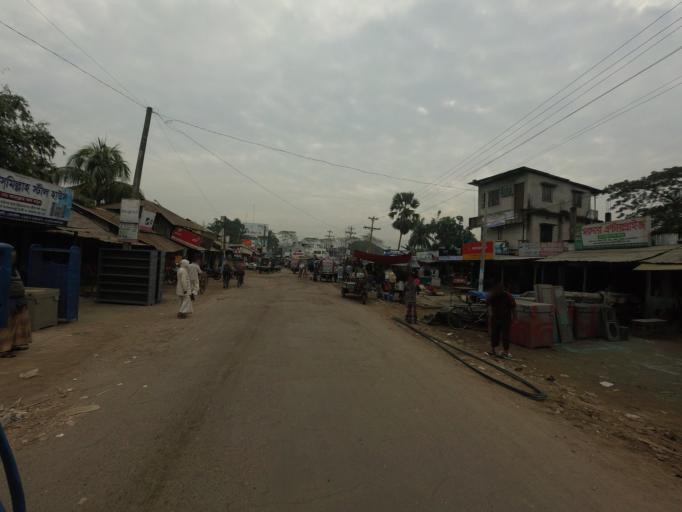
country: BD
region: Barisal
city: Nalchiti
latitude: 22.4646
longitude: 90.3794
